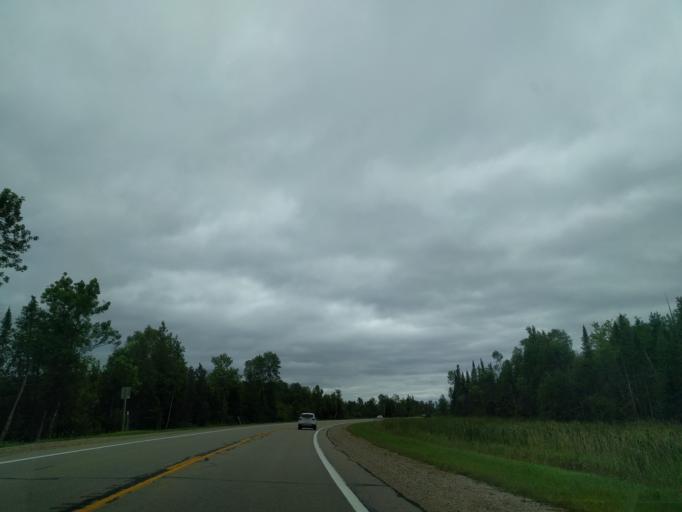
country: US
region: Michigan
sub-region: Menominee County
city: Menominee
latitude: 45.4200
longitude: -87.3467
